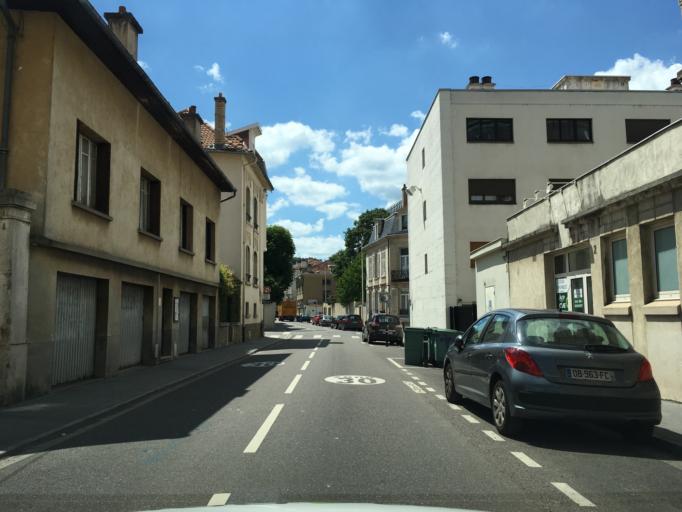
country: FR
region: Lorraine
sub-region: Departement de Meurthe-et-Moselle
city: Maxeville
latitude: 48.6982
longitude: 6.1736
